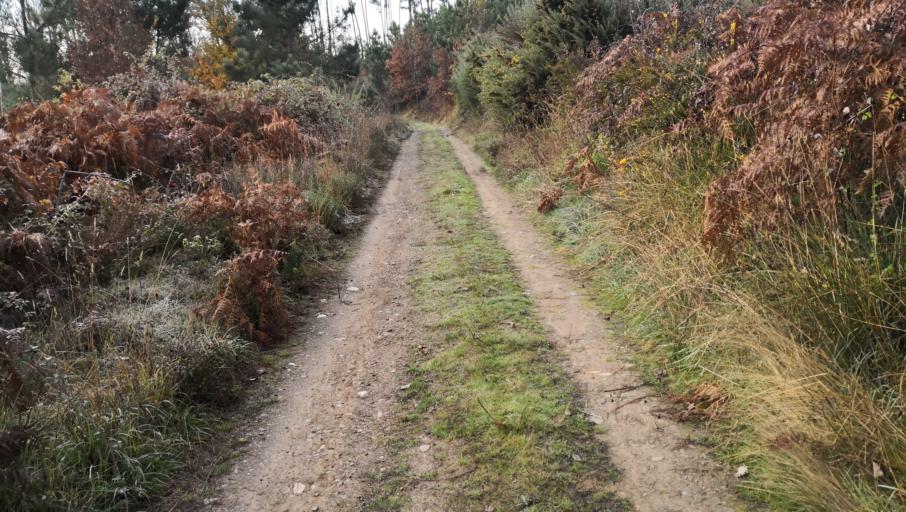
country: PT
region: Vila Real
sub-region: Sabrosa
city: Vilela
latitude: 41.2553
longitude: -7.6312
